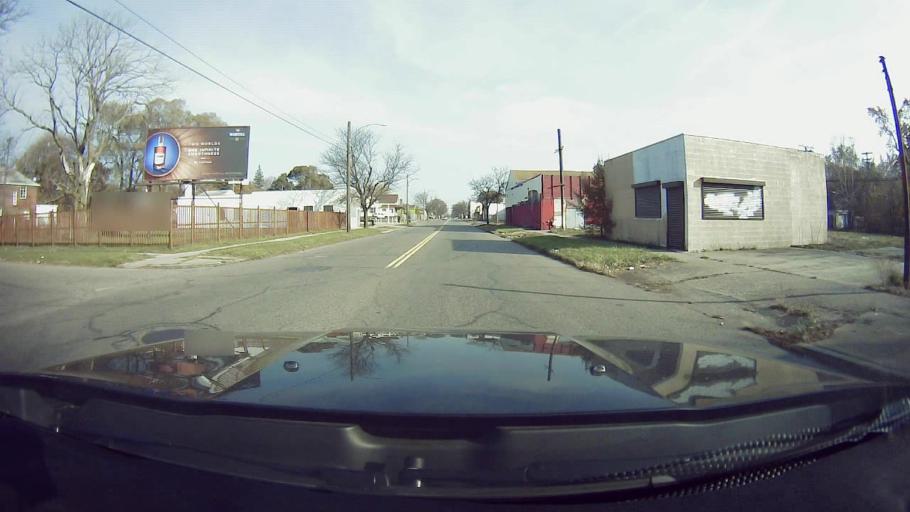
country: US
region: Michigan
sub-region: Wayne County
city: Highland Park
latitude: 42.4100
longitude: -83.1326
